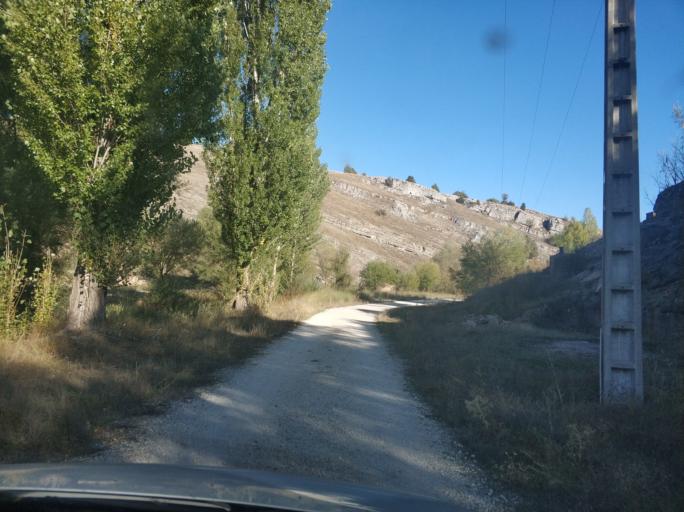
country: ES
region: Castille and Leon
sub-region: Provincia de Burgos
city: Hontoria del Pinar
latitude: 41.8439
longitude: -3.1624
